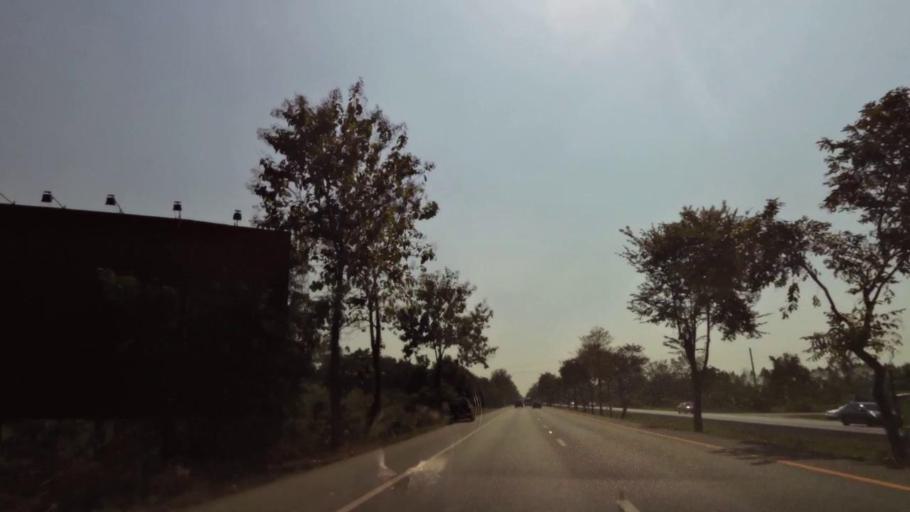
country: TH
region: Phichit
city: Bueng Na Rang
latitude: 16.0785
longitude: 100.1244
